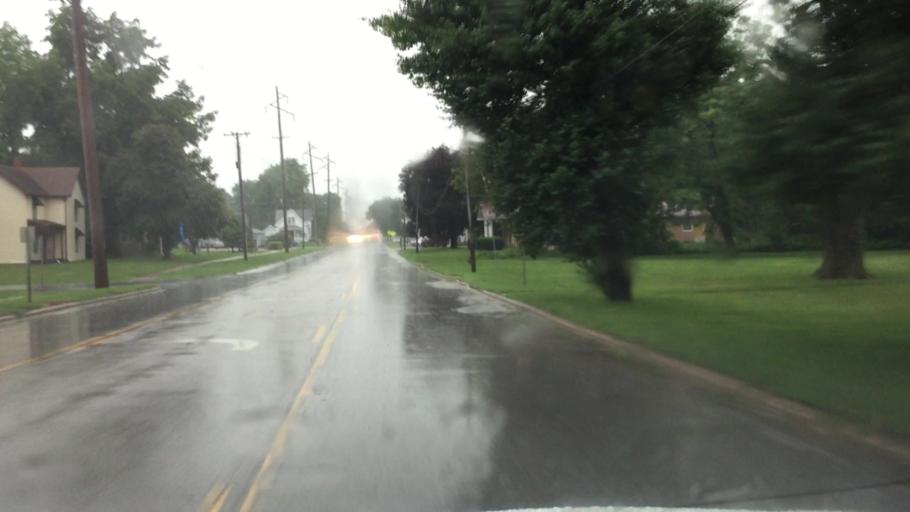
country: US
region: Illinois
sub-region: Hancock County
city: Carthage
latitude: 40.4162
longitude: -91.1282
